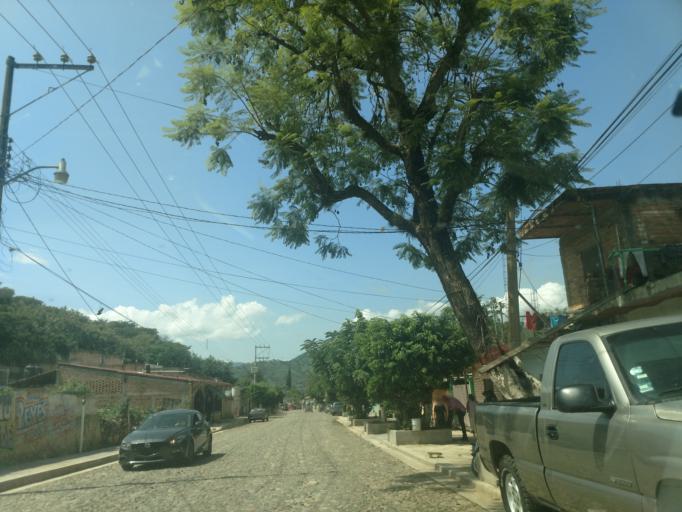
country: MX
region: Jalisco
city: Talpa de Allende
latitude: 20.3921
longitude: -104.8203
